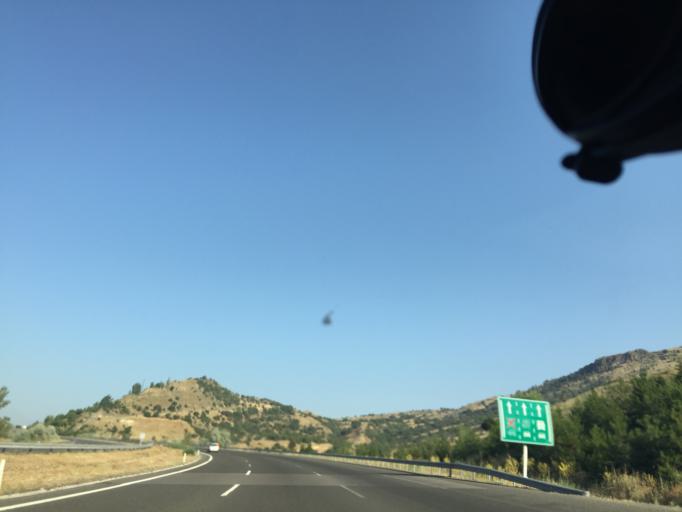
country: TR
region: Ankara
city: Celtikci
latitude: 40.3796
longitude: 32.4683
